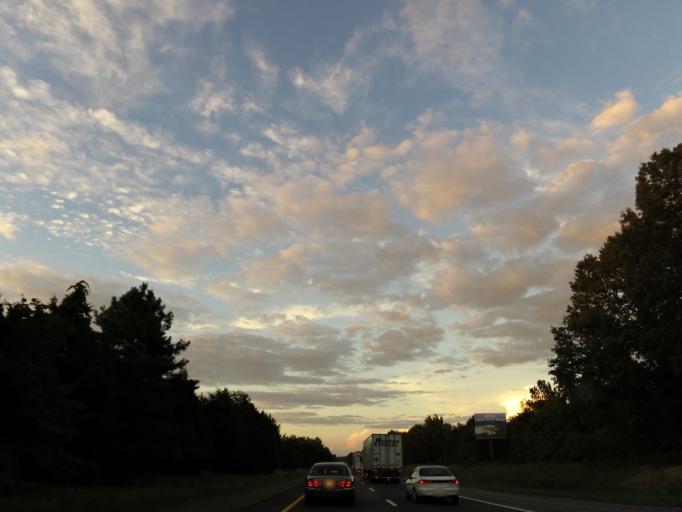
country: US
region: Tennessee
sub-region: Monroe County
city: Sweetwater
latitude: 35.6041
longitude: -84.5110
